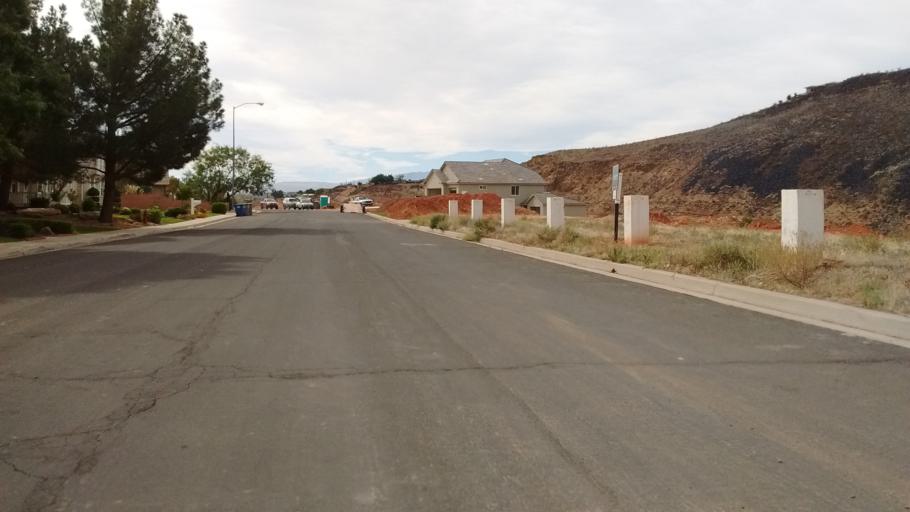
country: US
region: Utah
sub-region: Washington County
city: Washington
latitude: 37.1228
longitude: -113.4923
